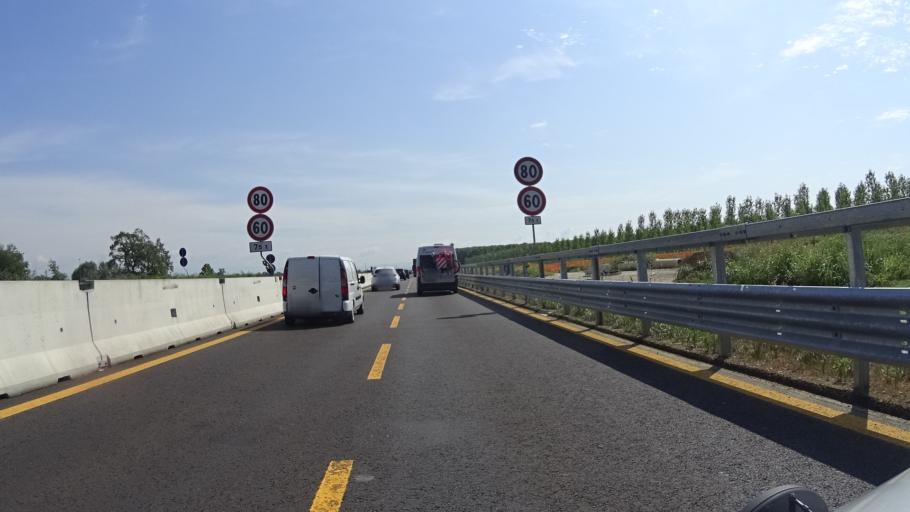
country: IT
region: Friuli Venezia Giulia
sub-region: Provincia di Udine
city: Gonars
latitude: 45.8752
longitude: 13.2416
